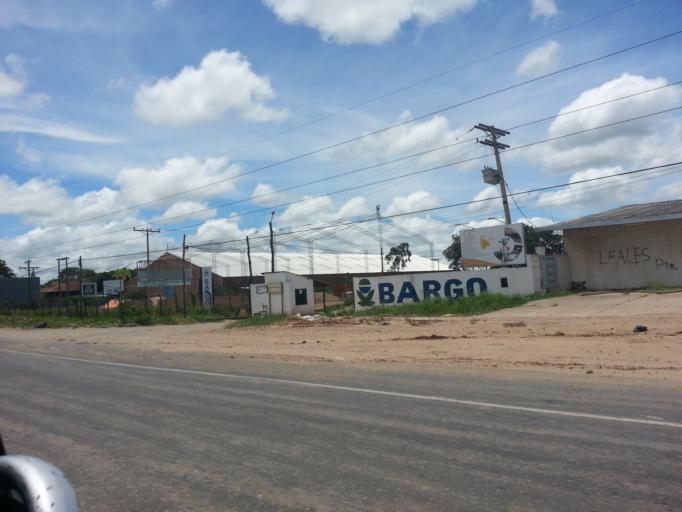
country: BO
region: Santa Cruz
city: Santa Cruz de la Sierra
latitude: -17.6904
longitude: -63.1592
